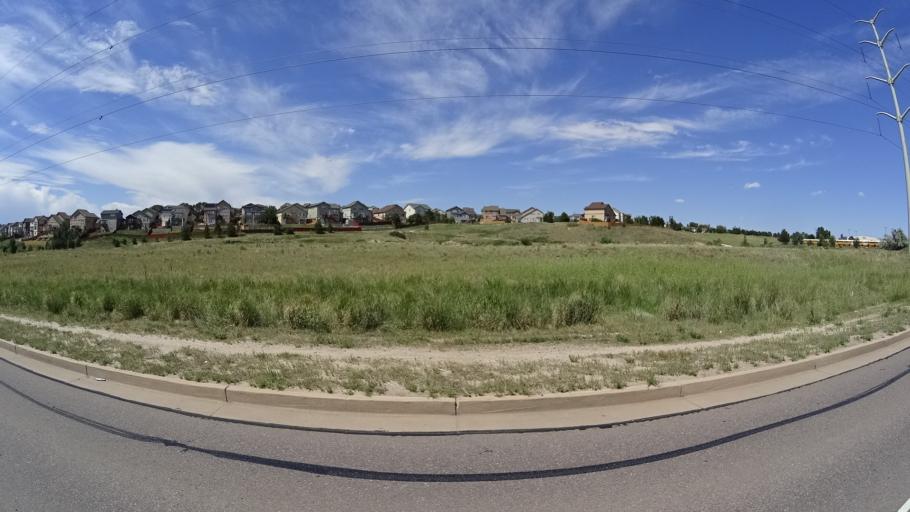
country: US
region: Colorado
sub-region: El Paso County
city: Black Forest
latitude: 38.9400
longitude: -104.7348
